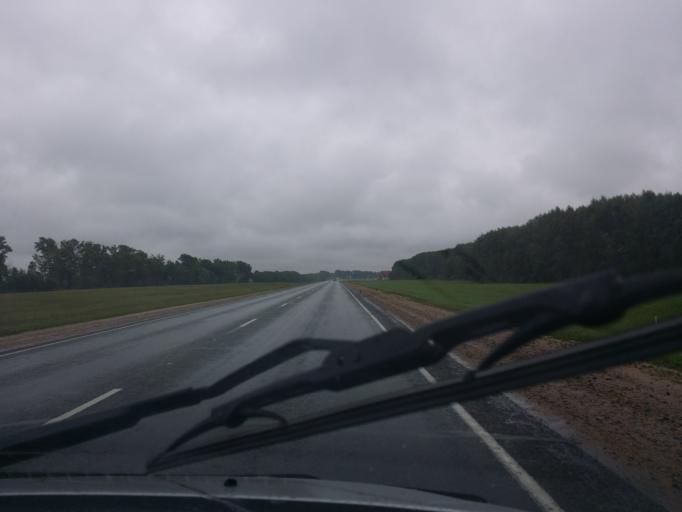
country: RU
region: Altai Krai
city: Bayunovskiye Klyuchi
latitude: 53.2919
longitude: 84.3105
